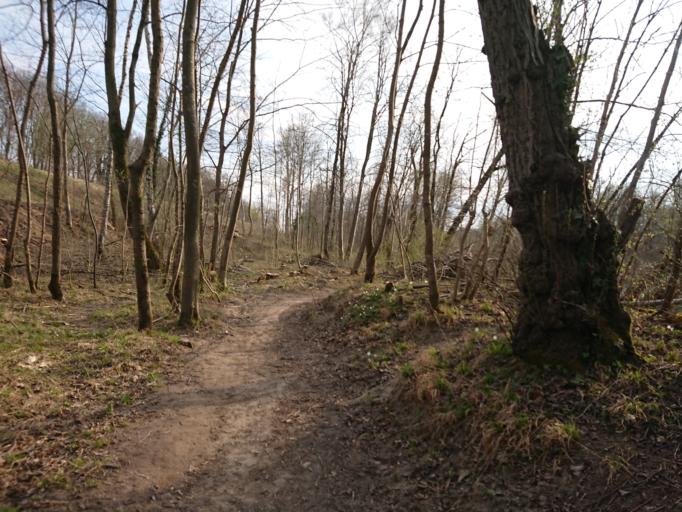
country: DE
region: Bavaria
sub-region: Upper Bavaria
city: Unterfoehring
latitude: 48.1824
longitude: 11.6290
